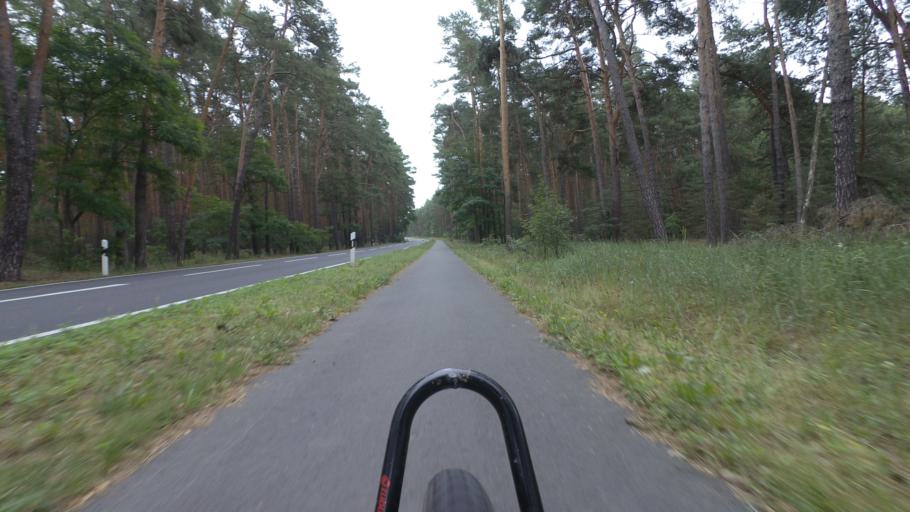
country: DE
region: Brandenburg
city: Sperenberg
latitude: 52.0879
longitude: 13.2752
